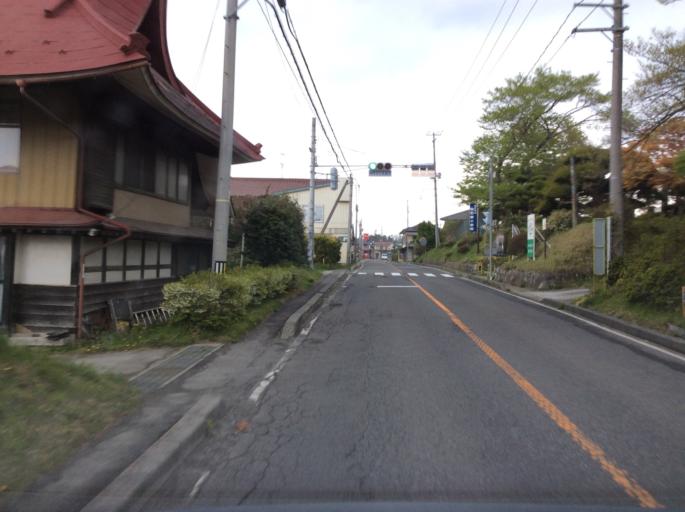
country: JP
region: Fukushima
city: Funehikimachi-funehiki
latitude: 37.3965
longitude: 140.5706
